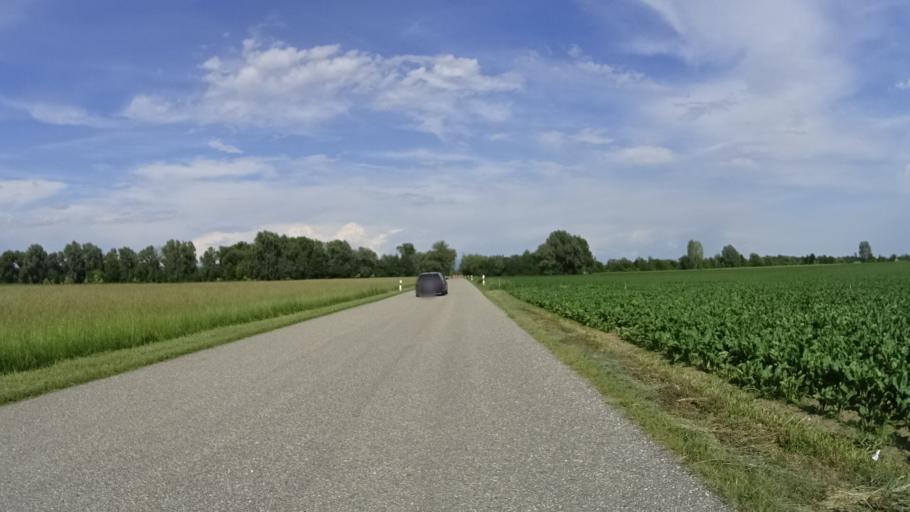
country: DE
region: Bavaria
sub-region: Lower Bavaria
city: Kirchroth
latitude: 48.9405
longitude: 12.5277
